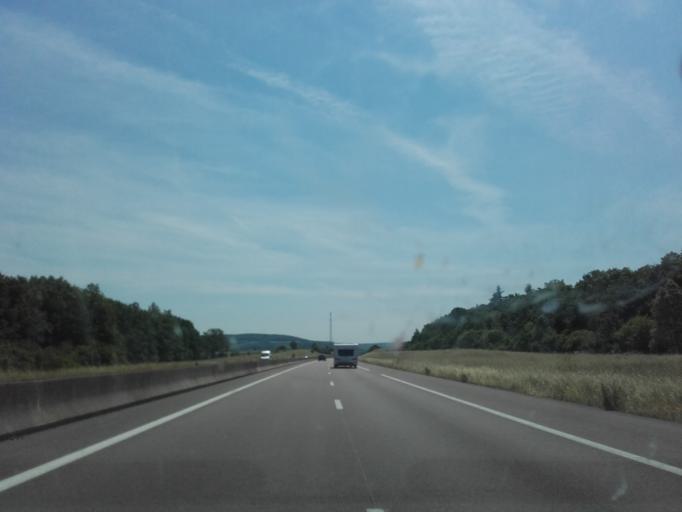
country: FR
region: Bourgogne
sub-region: Departement de la Cote-d'Or
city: Vitteaux
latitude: 47.3508
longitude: 4.4506
